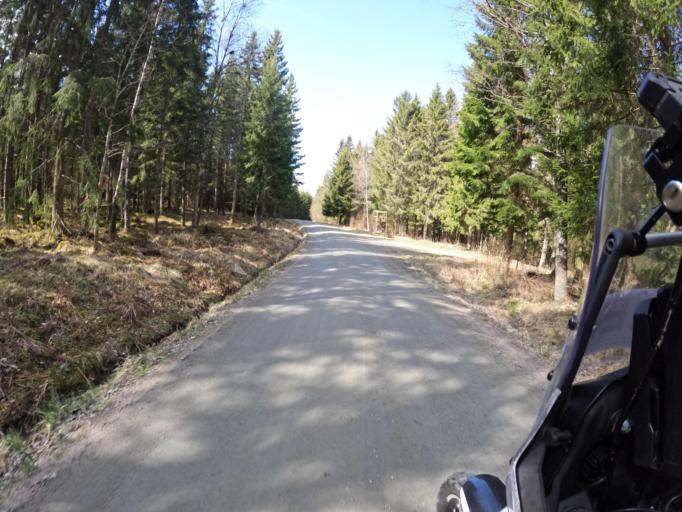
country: SE
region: Vaestra Goetaland
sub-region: Ulricehamns Kommun
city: Ulricehamn
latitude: 57.9196
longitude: 13.5096
